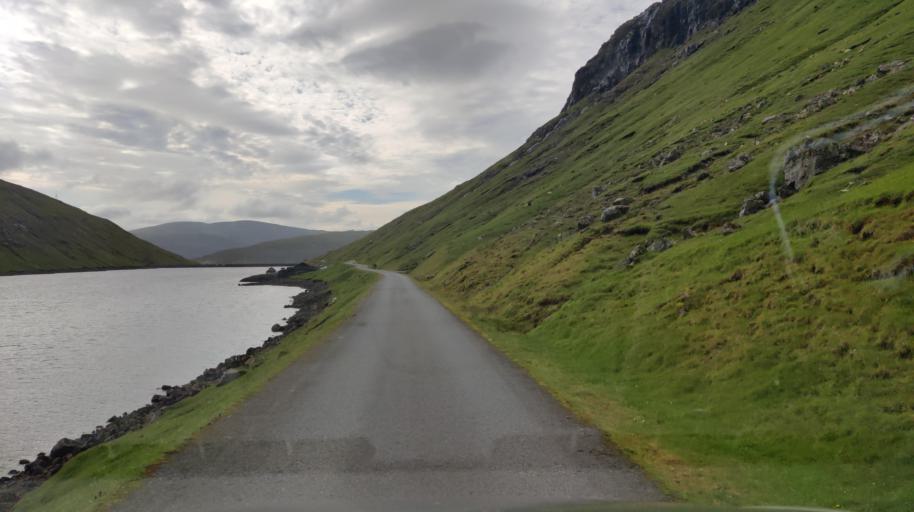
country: FO
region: Streymoy
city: Vestmanna
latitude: 62.1550
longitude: -7.1142
